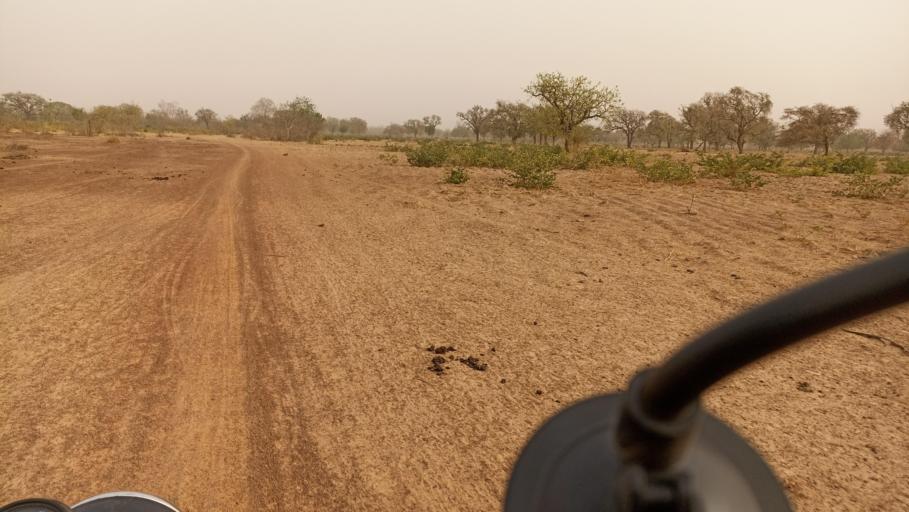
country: BF
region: Boucle du Mouhoun
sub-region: Province du Nayala
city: Toma
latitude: 12.8714
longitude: -2.7551
